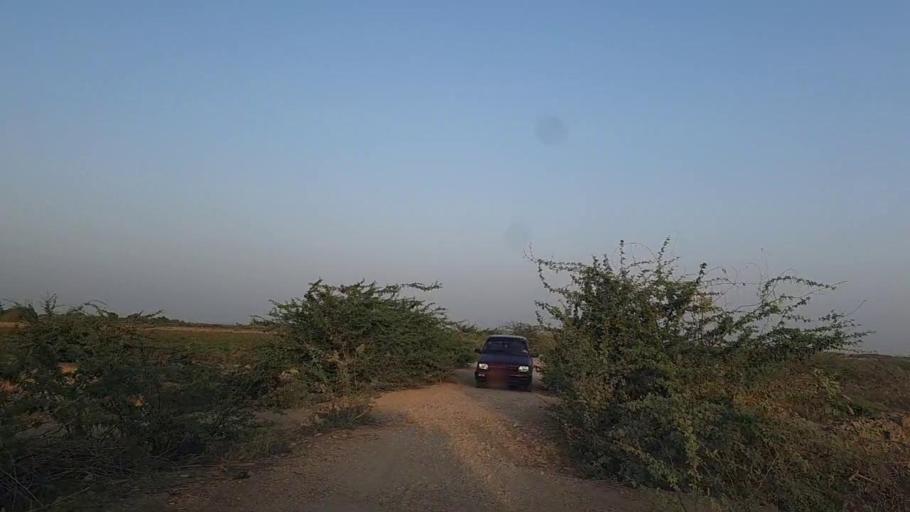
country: PK
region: Sindh
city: Naukot
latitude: 24.6981
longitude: 69.2571
